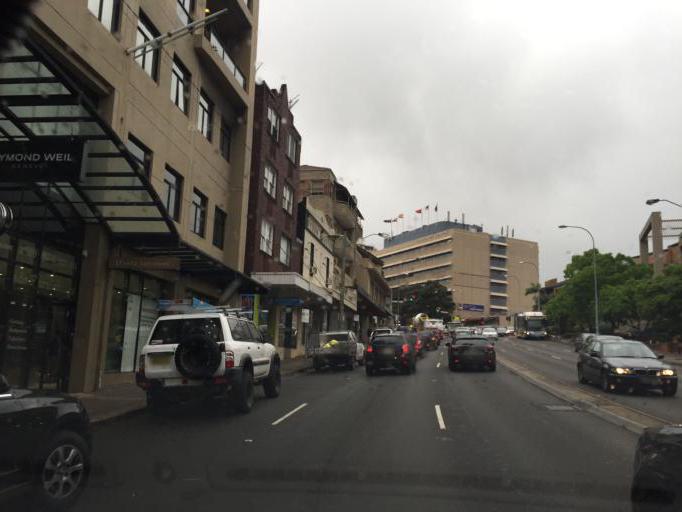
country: AU
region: New South Wales
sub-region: Woollahra
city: Paddington
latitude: -33.8777
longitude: 151.2343
